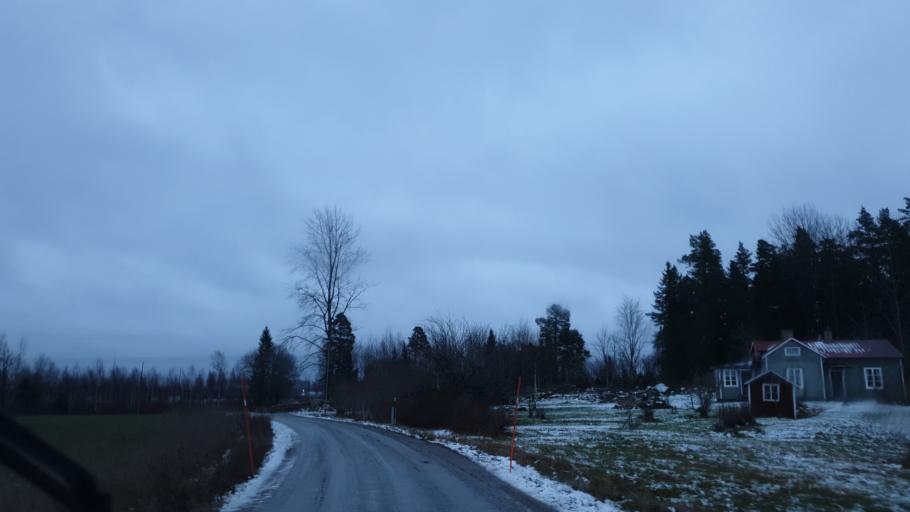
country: SE
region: Uppsala
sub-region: Tierps Kommun
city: Tierp
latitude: 60.3394
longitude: 17.4772
